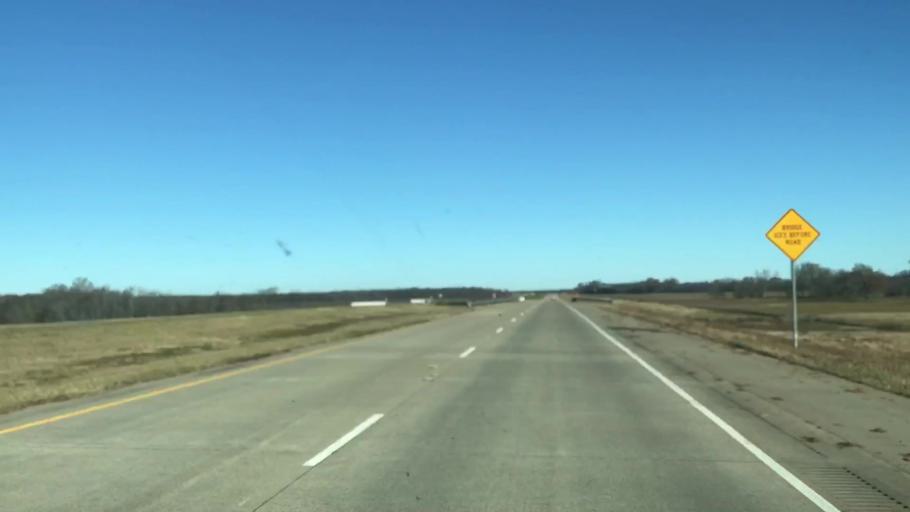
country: US
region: Louisiana
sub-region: Caddo Parish
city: Blanchard
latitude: 32.6292
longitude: -93.8370
